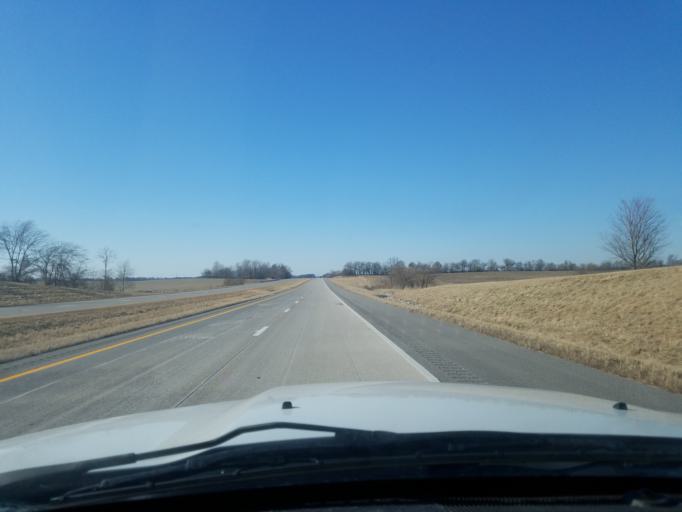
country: US
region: Kentucky
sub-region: Henderson County
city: Henderson
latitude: 37.7946
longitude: -87.4967
